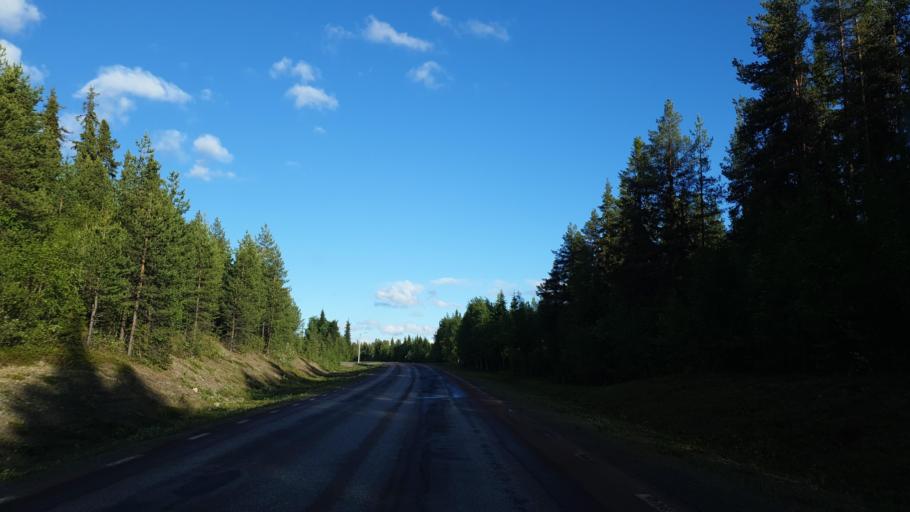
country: SE
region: Norrbotten
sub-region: Arjeplogs Kommun
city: Arjeplog
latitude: 66.0150
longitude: 18.0825
